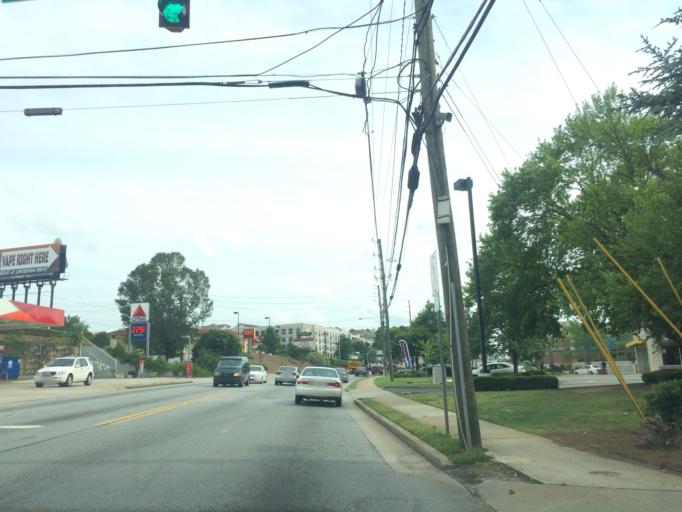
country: US
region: Georgia
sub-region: DeKalb County
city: North Druid Hills
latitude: 33.8205
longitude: -84.3514
